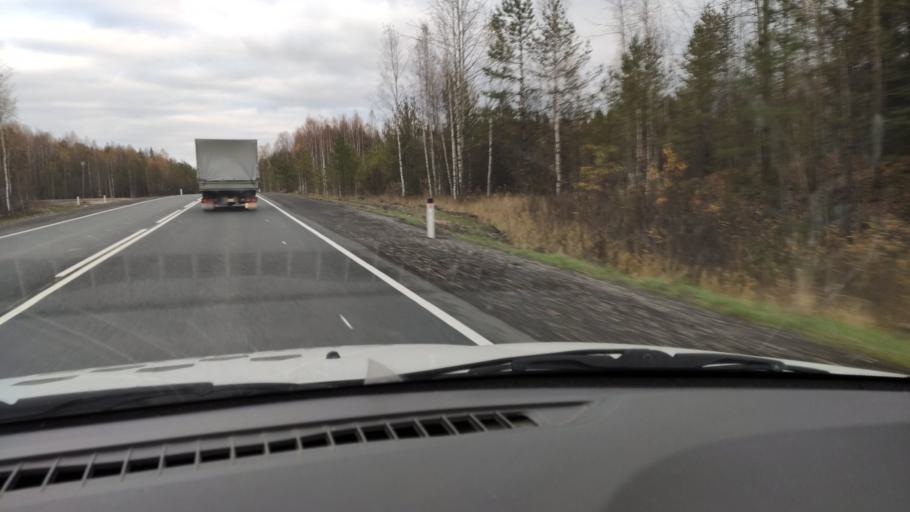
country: RU
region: Kirov
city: Chernaya Kholunitsa
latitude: 58.8738
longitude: 51.5043
